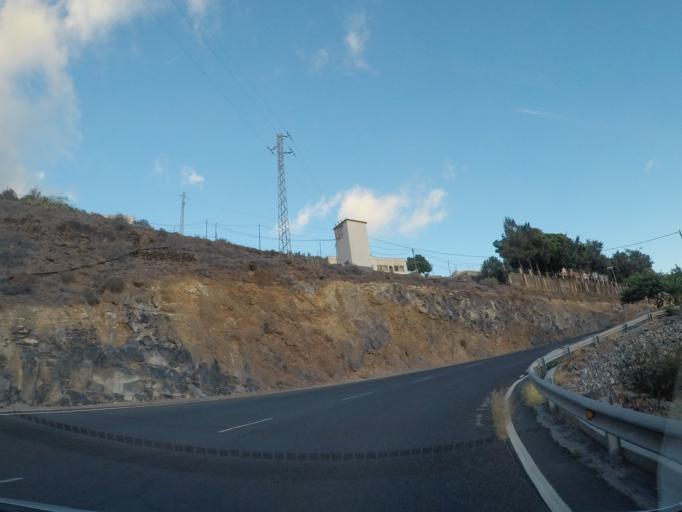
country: ES
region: Canary Islands
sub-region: Provincia de Santa Cruz de Tenerife
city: Alajero
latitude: 28.0337
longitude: -17.1929
